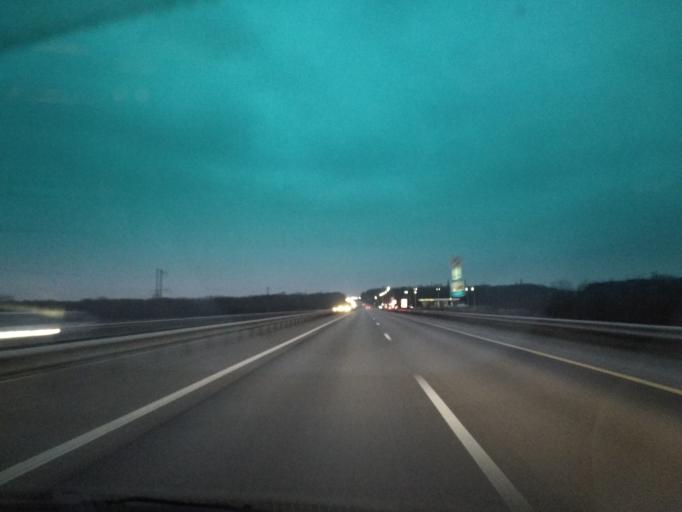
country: RU
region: Krasnodarskiy
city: Saratovskaya
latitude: 44.7956
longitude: 39.2325
